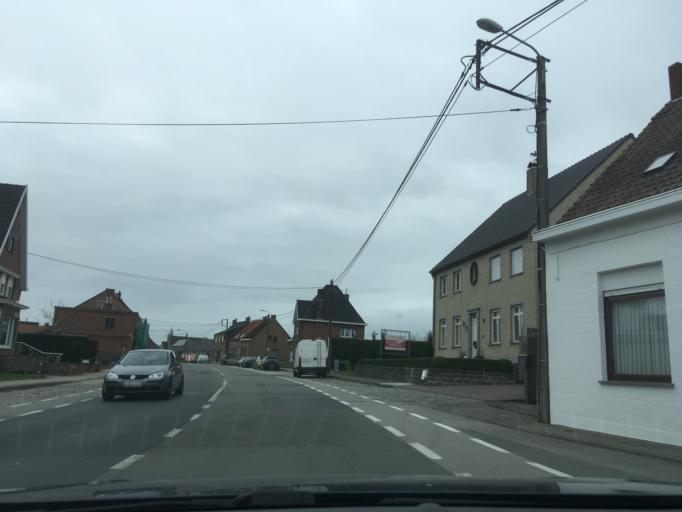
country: BE
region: Flanders
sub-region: Provincie West-Vlaanderen
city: Kortemark
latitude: 51.0287
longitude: 3.0569
